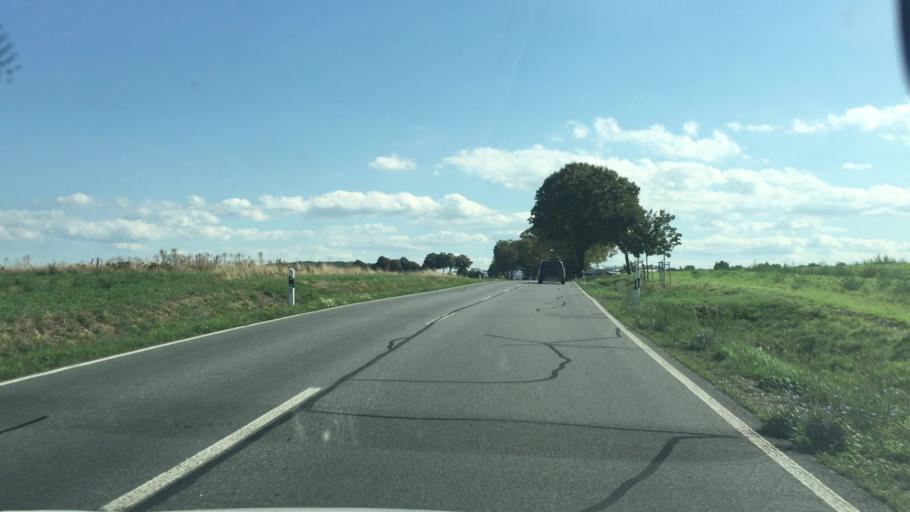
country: DE
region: Saxony
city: Dohma
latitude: 50.9265
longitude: 13.9315
